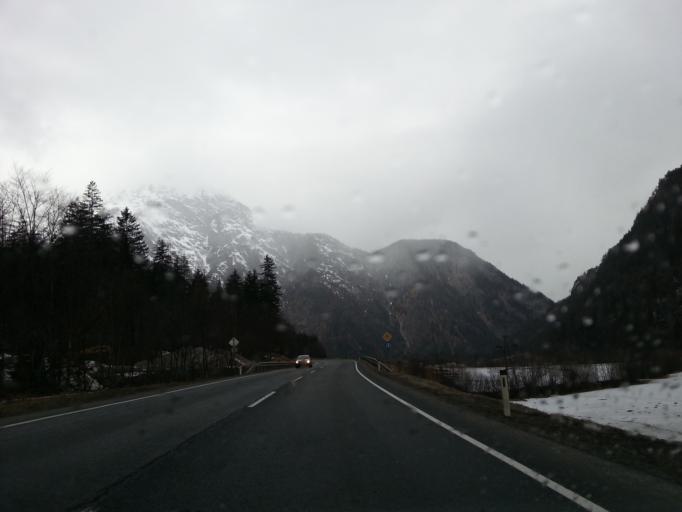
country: AT
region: Salzburg
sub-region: Politischer Bezirk Zell am See
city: Sankt Martin bei Lofer
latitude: 47.5279
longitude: 12.7367
